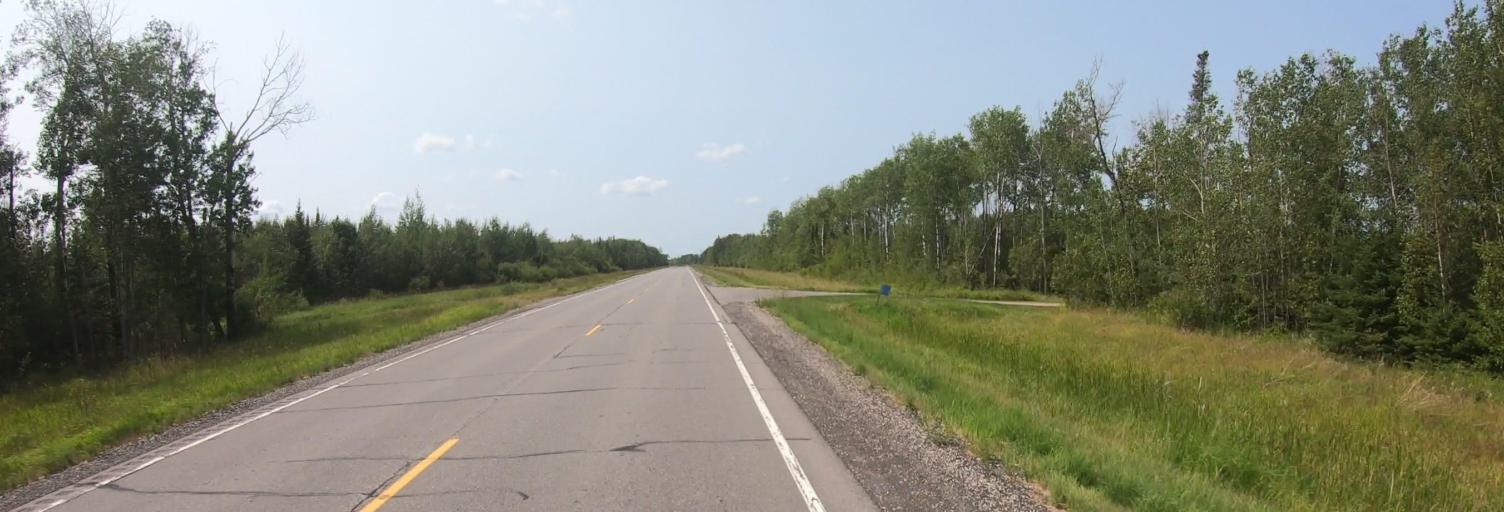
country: US
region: Minnesota
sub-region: Lake of the Woods County
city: Baudette
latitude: 48.6996
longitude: -94.3969
